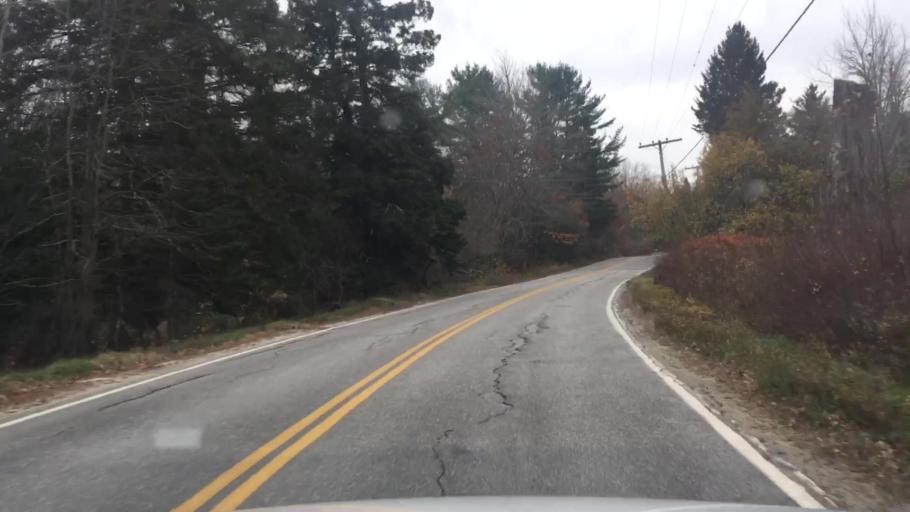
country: US
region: Maine
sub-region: Hancock County
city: Sedgwick
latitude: 44.2913
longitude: -68.5549
